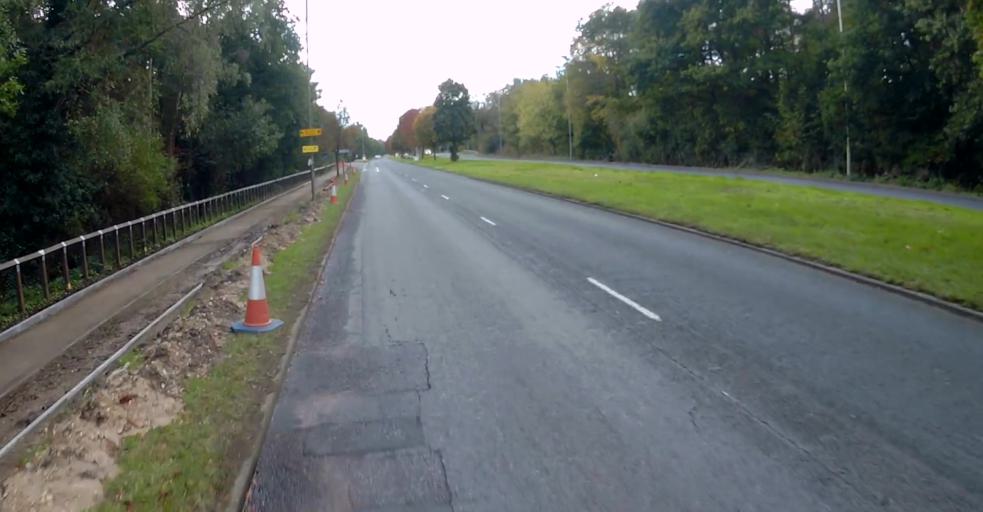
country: GB
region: England
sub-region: Hampshire
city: Aldershot
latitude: 51.2646
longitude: -0.7642
